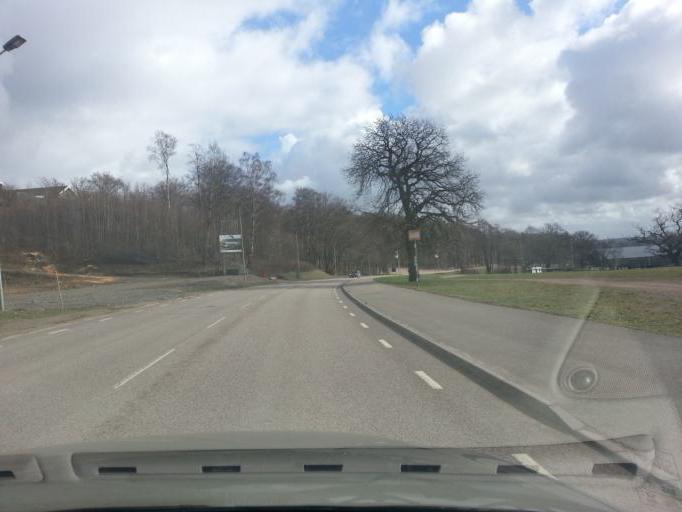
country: SE
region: Skane
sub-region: Astorps Kommun
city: Astorp
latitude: 56.1257
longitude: 12.9511
